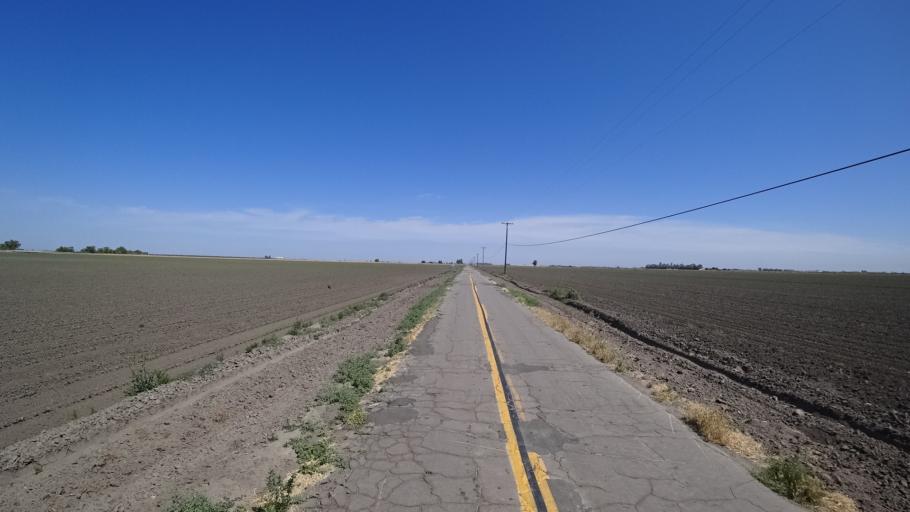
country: US
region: California
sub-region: Kings County
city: Stratford
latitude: 36.1972
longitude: -119.8162
